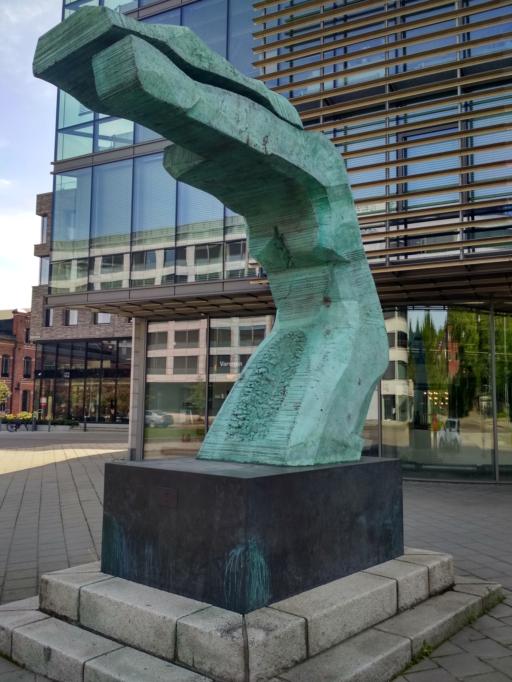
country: NO
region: Oslo
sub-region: Oslo
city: Sjolyststranda
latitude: 59.9221
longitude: 10.6862
